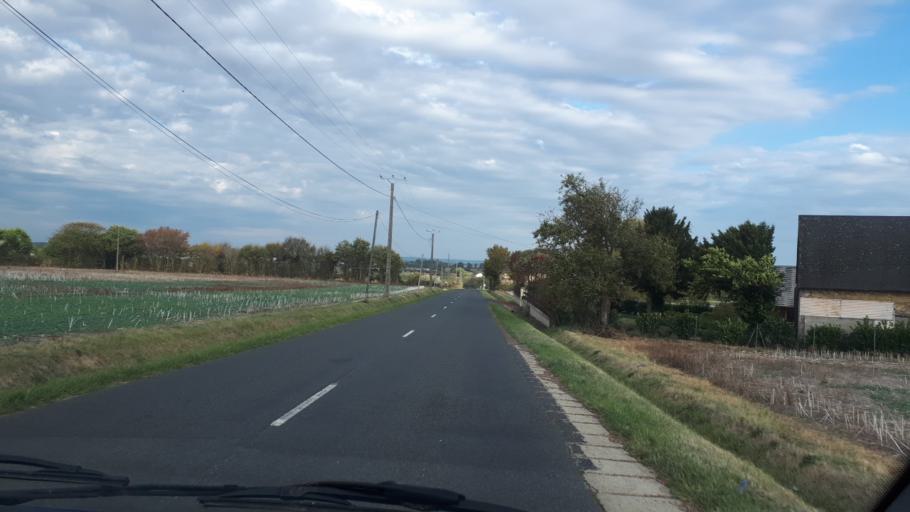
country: FR
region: Centre
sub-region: Departement du Loir-et-Cher
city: Mondoubleau
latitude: 47.9675
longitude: 0.9252
